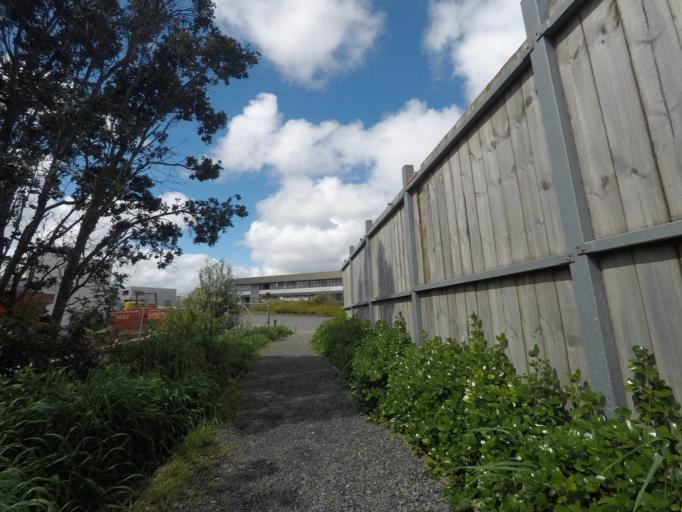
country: NZ
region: Auckland
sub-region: Auckland
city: Rosebank
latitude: -36.8774
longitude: 174.6660
